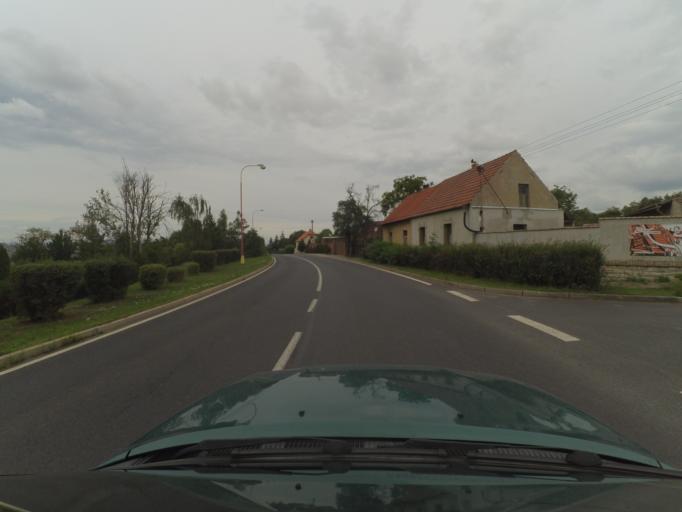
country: CZ
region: Ustecky
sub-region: Okres Louny
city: Louny
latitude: 50.3147
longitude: 13.8032
